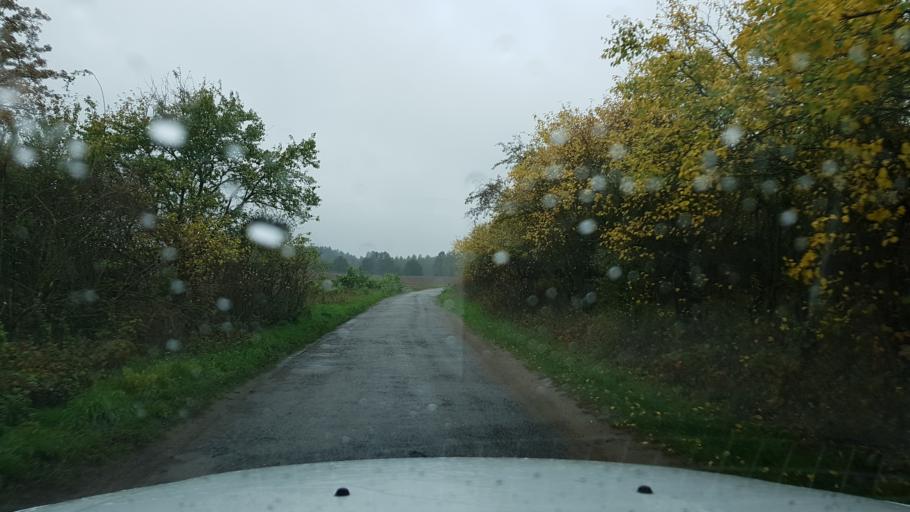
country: PL
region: West Pomeranian Voivodeship
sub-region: Powiat mysliborski
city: Barlinek
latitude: 53.0412
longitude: 15.2406
